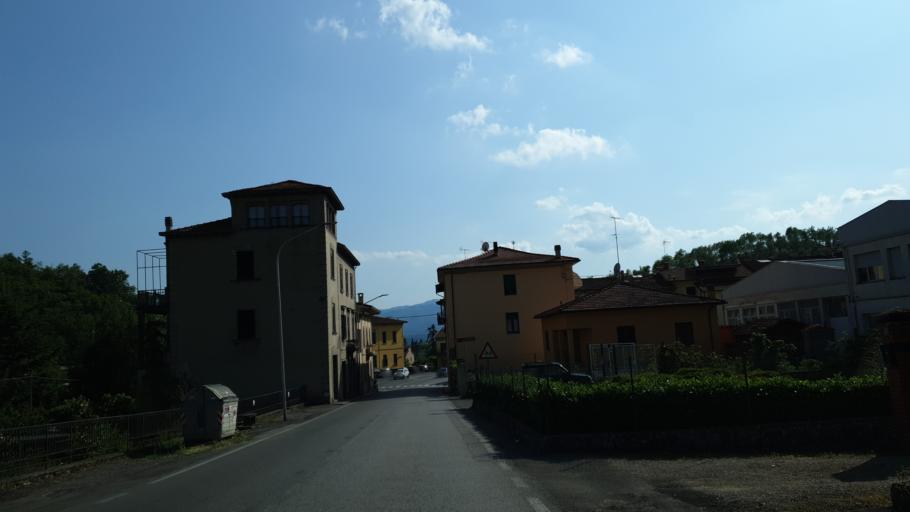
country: IT
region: Tuscany
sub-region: Province of Arezzo
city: Soci
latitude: 43.7506
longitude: 11.8236
